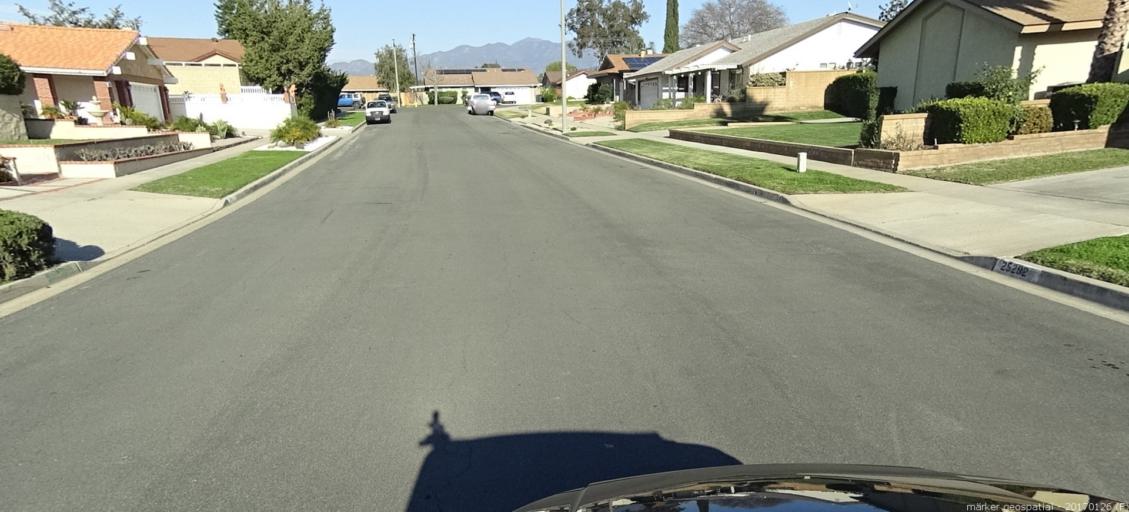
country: US
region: California
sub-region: Orange County
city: Lake Forest
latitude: 33.6337
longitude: -117.6892
